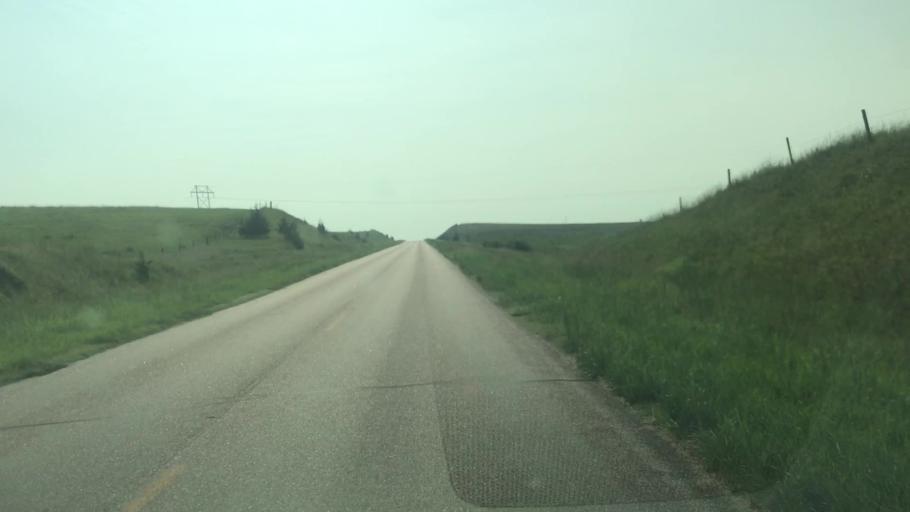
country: US
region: Nebraska
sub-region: Sherman County
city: Loup City
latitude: 41.2793
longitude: -98.9381
